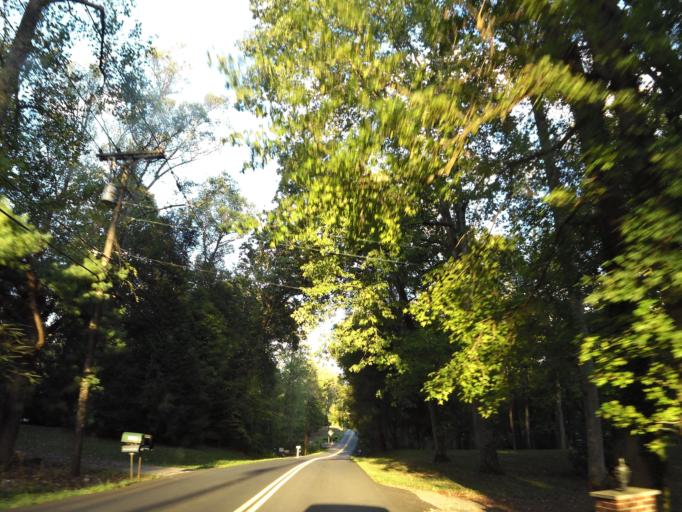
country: US
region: Tennessee
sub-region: Knox County
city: Knoxville
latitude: 35.9055
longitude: -83.9496
